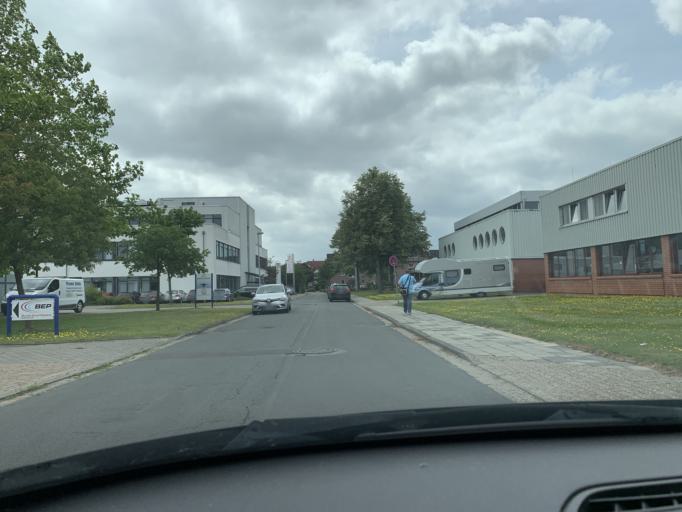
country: DE
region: Lower Saxony
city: Westerstede
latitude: 53.2606
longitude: 7.9371
